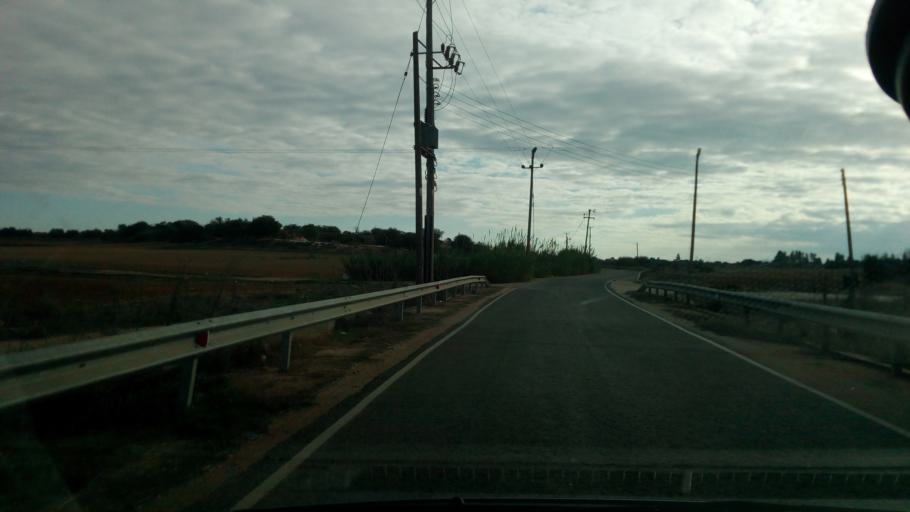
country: CY
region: Ammochostos
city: Frenaros
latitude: 35.0482
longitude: 33.8875
